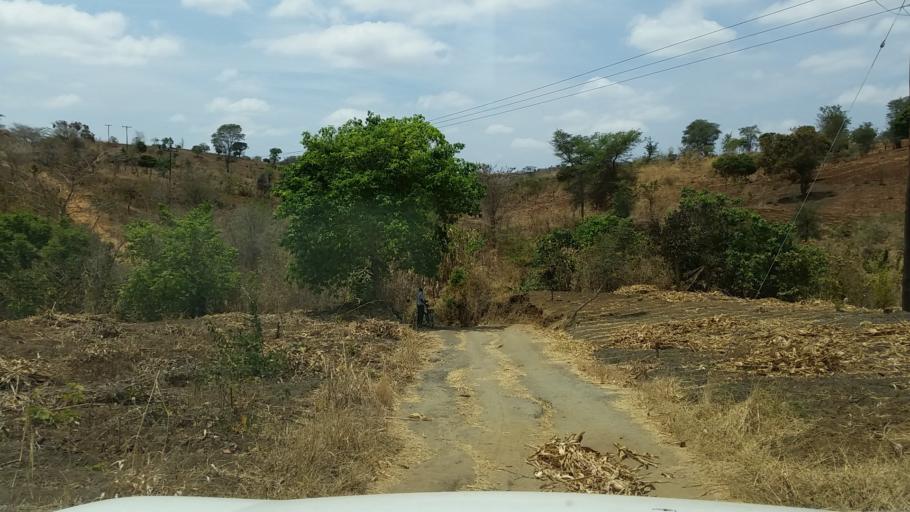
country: MW
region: Central Region
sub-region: Dowa District
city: Dowa
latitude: -13.7106
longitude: 34.0948
